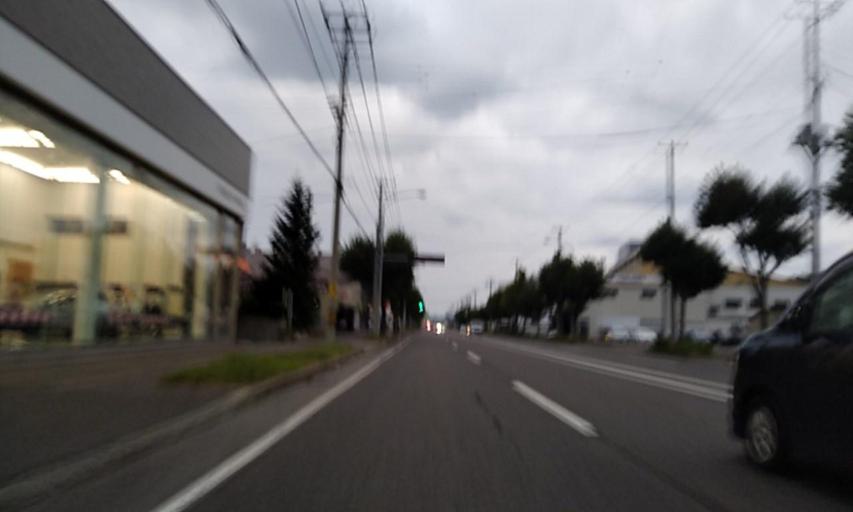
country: JP
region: Hokkaido
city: Abashiri
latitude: 44.0172
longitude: 144.2437
